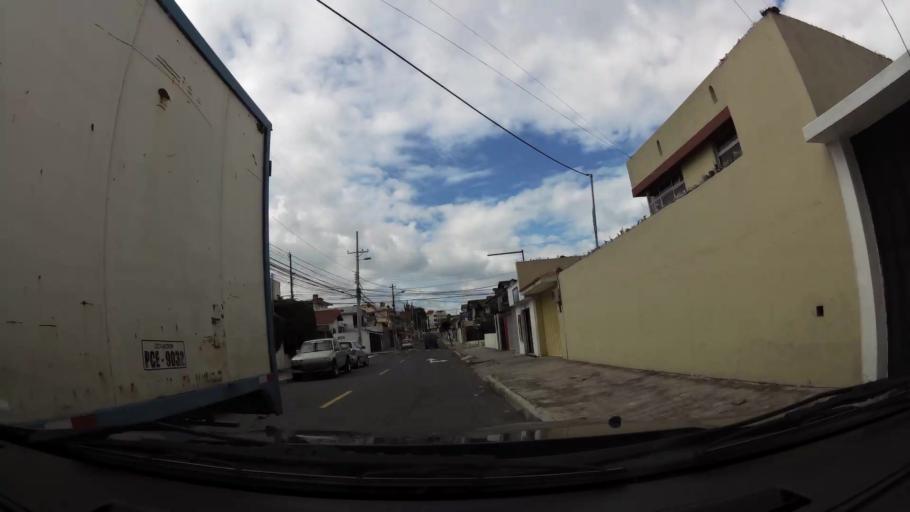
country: EC
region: Pichincha
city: Quito
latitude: -0.1605
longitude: -78.4815
